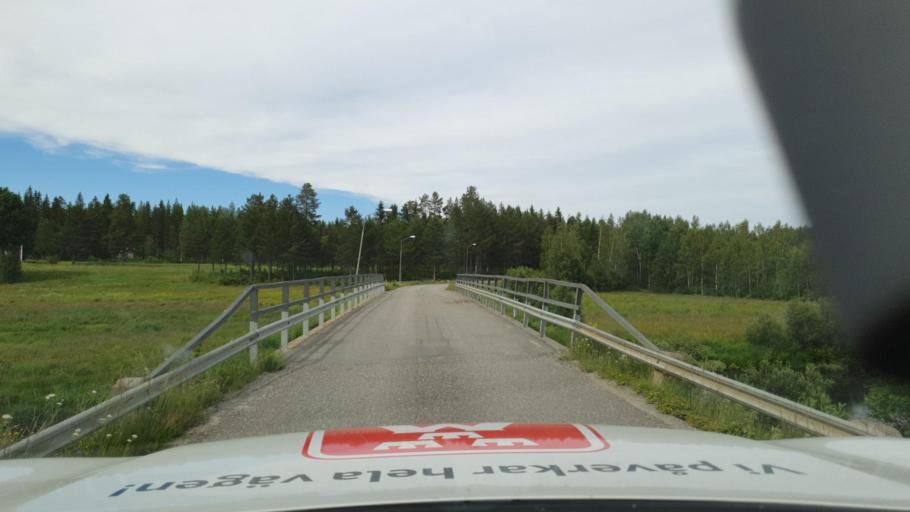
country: SE
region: Vaesterbotten
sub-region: Skelleftea Kommun
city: Viken
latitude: 64.5165
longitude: 20.9524
